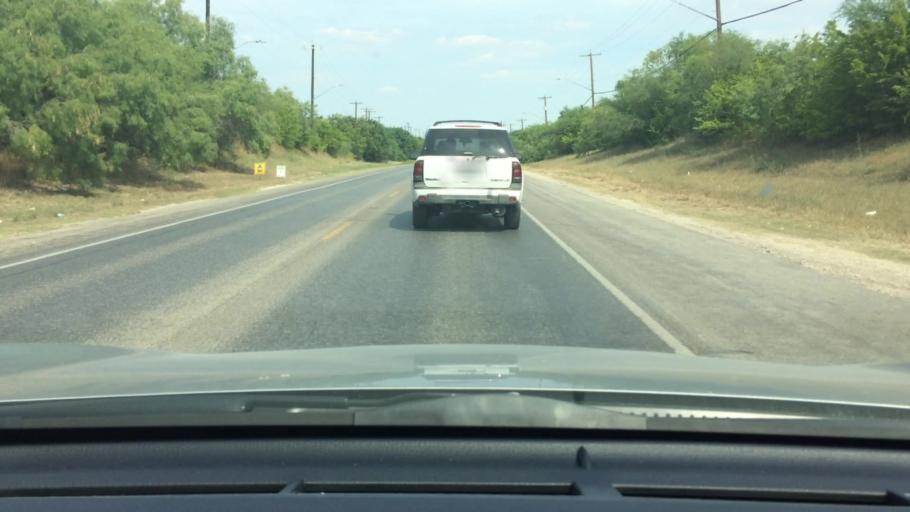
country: US
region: Texas
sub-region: Bexar County
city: San Antonio
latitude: 29.3329
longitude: -98.4485
